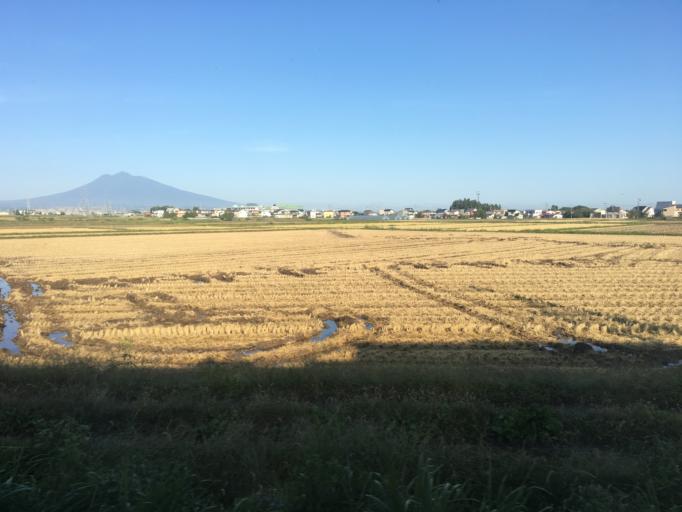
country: JP
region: Aomori
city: Kuroishi
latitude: 40.5817
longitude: 140.5597
